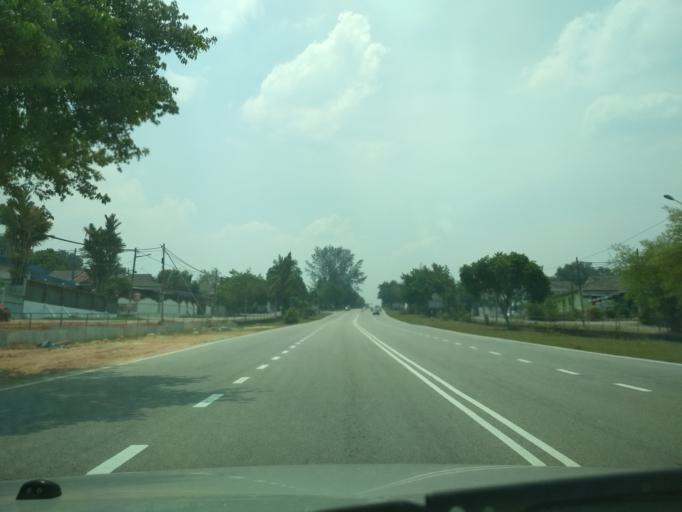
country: MY
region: Kedah
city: Kulim
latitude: 5.3553
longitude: 100.5306
